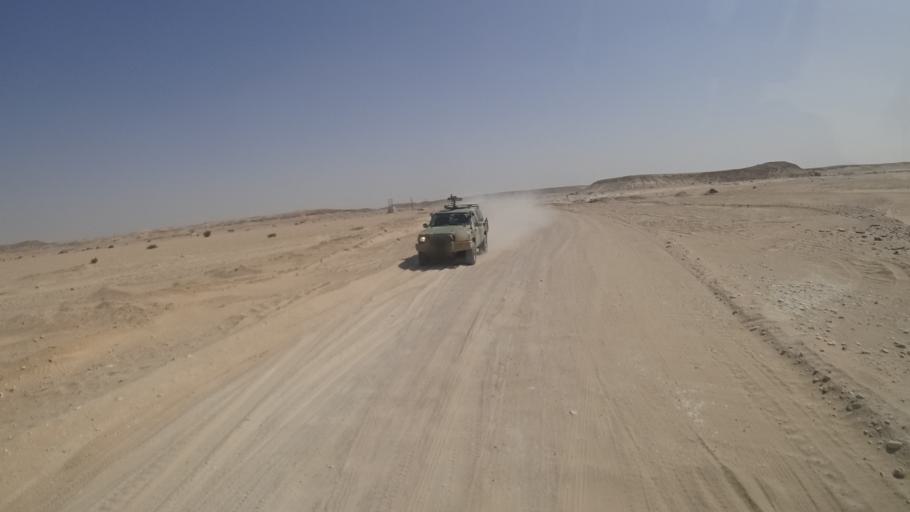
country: YE
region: Al Mahrah
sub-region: Shahan
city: Shihan as Sufla
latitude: 17.8746
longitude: 52.6071
